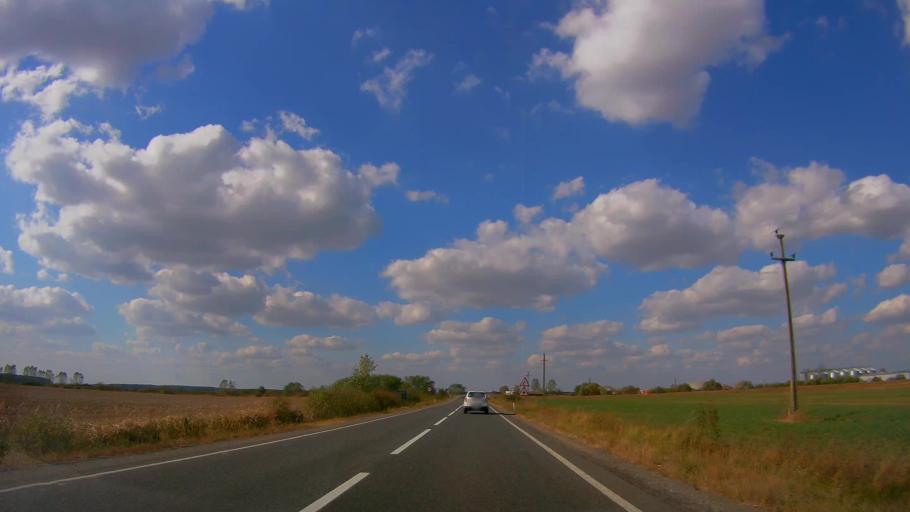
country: RO
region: Satu Mare
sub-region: Oras Ardud
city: Ardud
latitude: 47.6238
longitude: 22.8716
